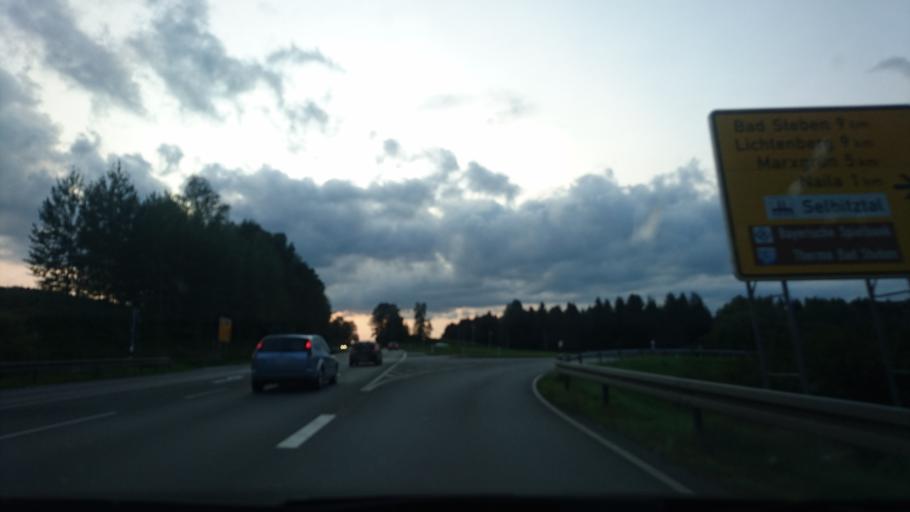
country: DE
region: Bavaria
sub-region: Upper Franconia
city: Naila
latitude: 50.3204
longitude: 11.7150
